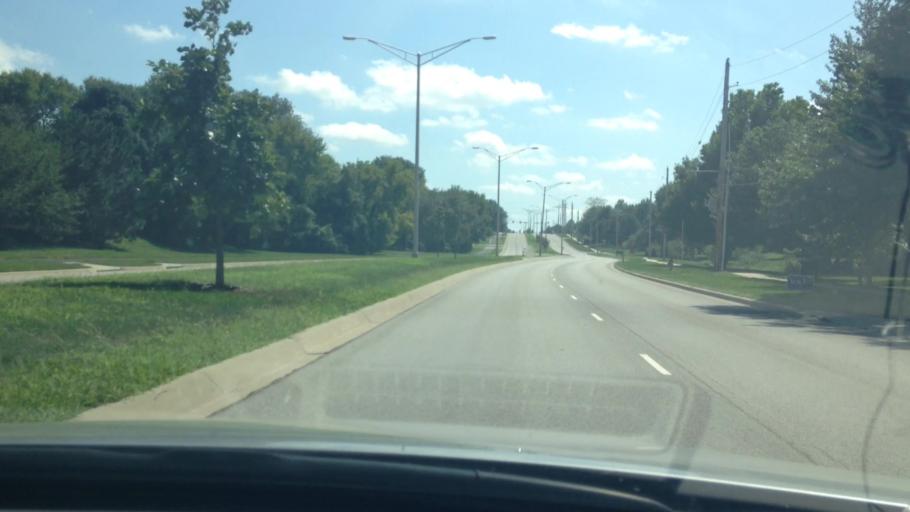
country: US
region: Kansas
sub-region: Johnson County
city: Lenexa
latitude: 38.8593
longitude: -94.7050
